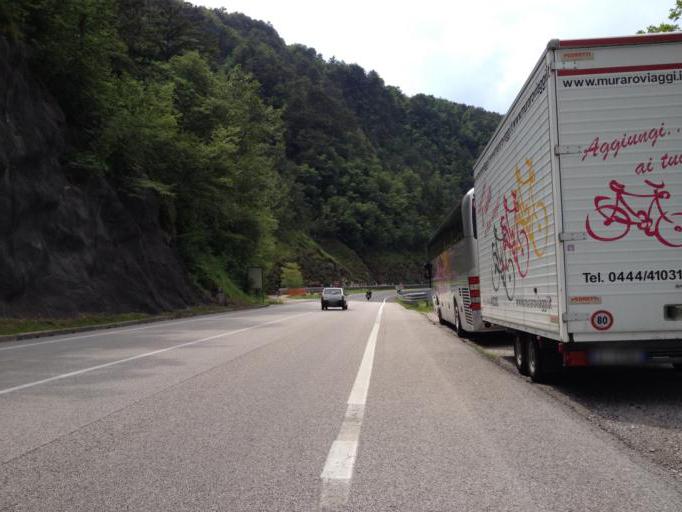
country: IT
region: Friuli Venezia Giulia
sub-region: Provincia di Udine
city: Moggio di Sotto
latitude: 46.3968
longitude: 13.1960
